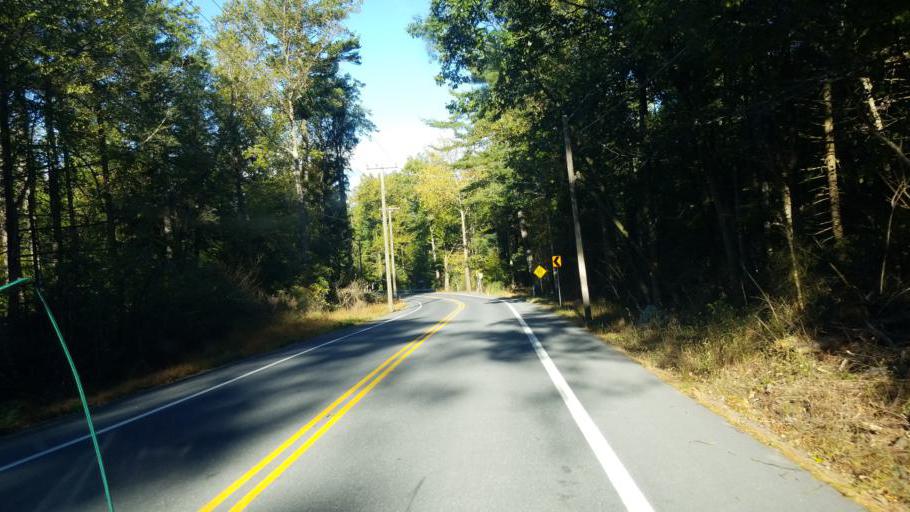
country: US
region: Pennsylvania
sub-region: Franklin County
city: Mont Alto
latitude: 39.8385
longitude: -77.5353
